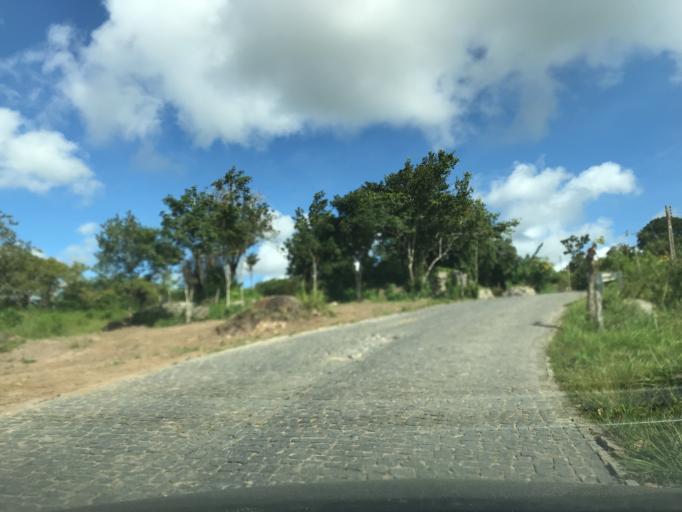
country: BR
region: Pernambuco
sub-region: Bezerros
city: Bezerros
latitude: -8.1760
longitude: -35.7693
